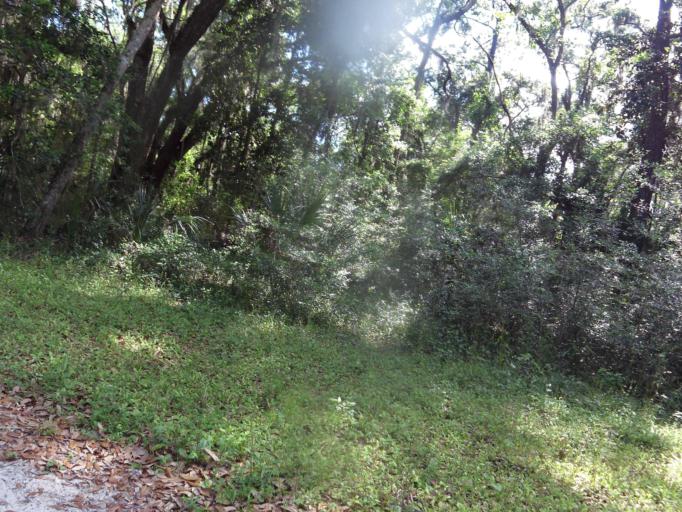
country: US
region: Florida
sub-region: Saint Johns County
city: Palm Valley
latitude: 30.1342
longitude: -81.3681
